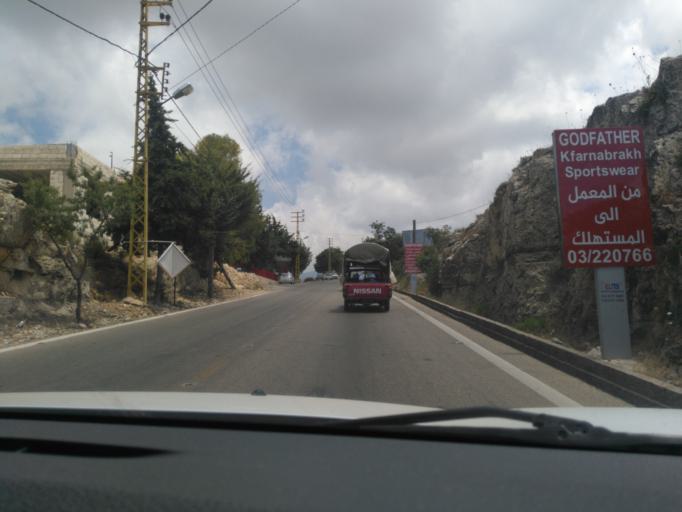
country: LB
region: Mont-Liban
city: Beit ed Dine
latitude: 33.6966
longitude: 35.6153
